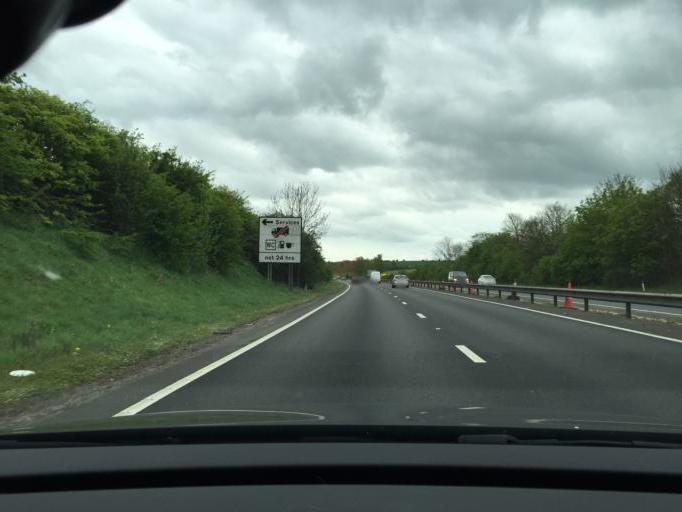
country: GB
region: England
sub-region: Oxfordshire
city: Harwell
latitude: 51.5649
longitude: -1.3016
